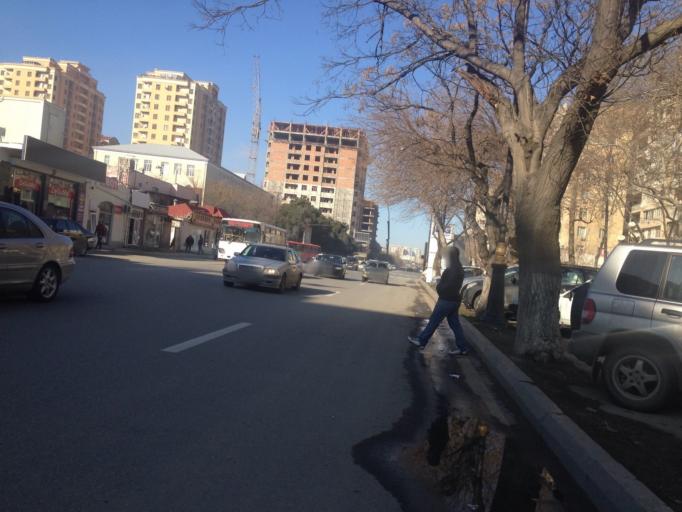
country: AZ
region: Baki
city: Bilajari
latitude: 40.3992
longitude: 49.8386
